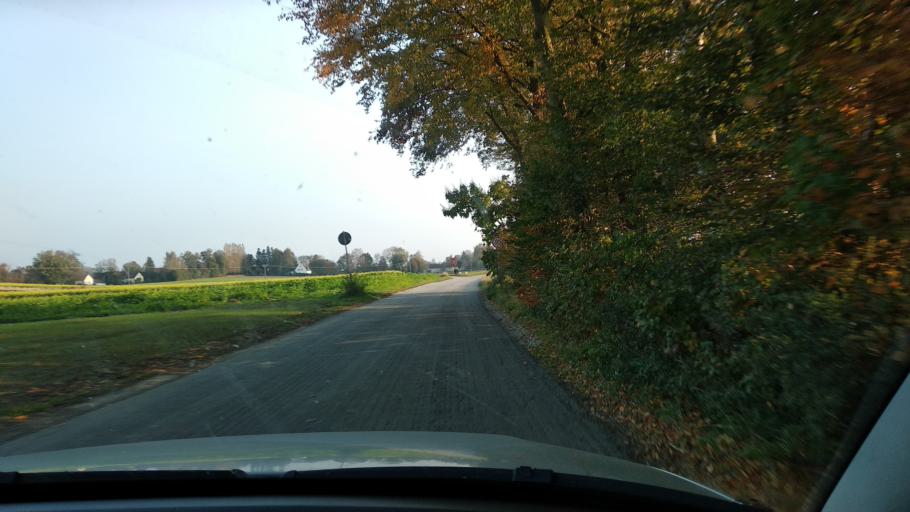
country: DE
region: Bavaria
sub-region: Upper Bavaria
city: Ottenhofen
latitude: 48.2072
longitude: 11.8920
